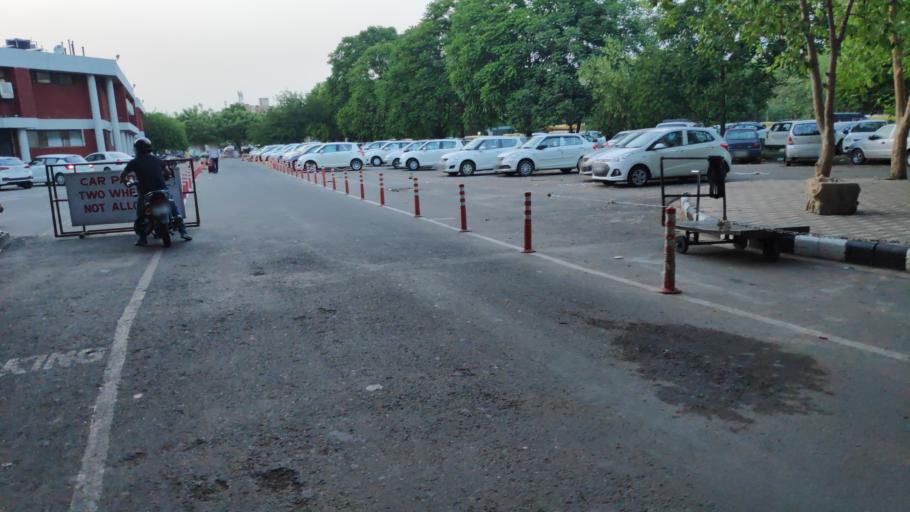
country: IN
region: Punjab
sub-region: Ajitgarh
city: Mohali
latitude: 30.7166
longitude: 76.7447
